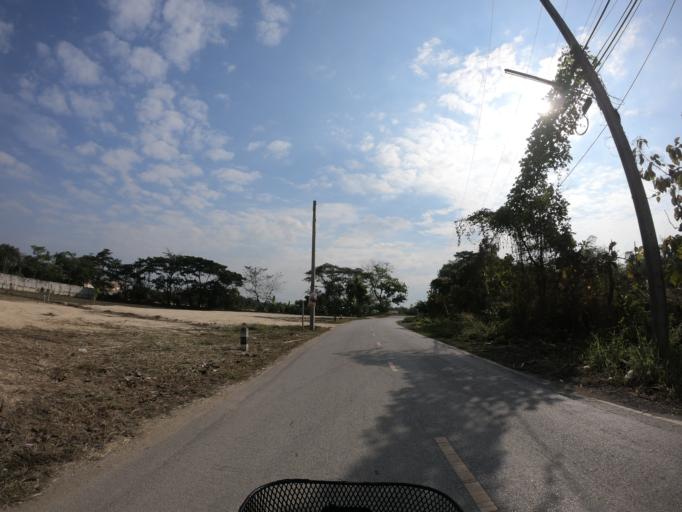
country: TH
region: Chiang Mai
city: San Sai
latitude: 18.8078
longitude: 99.0604
